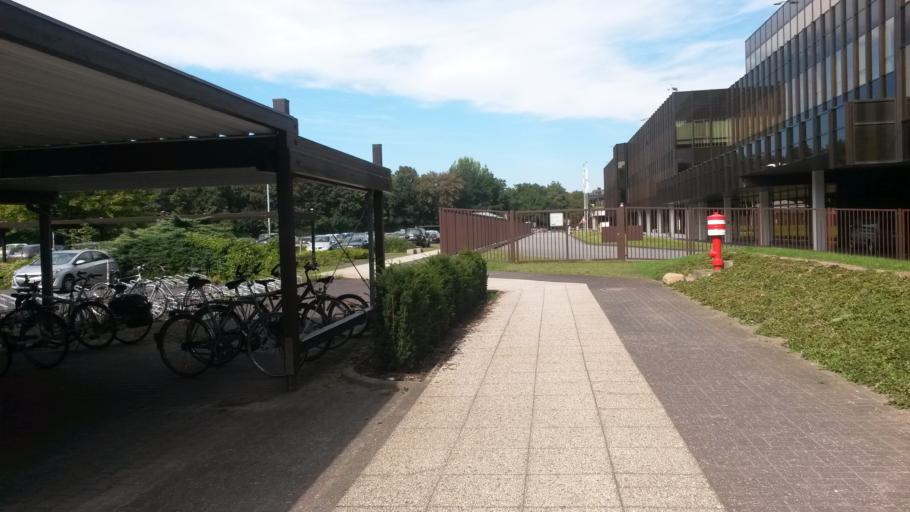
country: DE
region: North Rhine-Westphalia
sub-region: Regierungsbezirk Detmold
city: Paderborn
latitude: 51.7176
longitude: 8.7148
